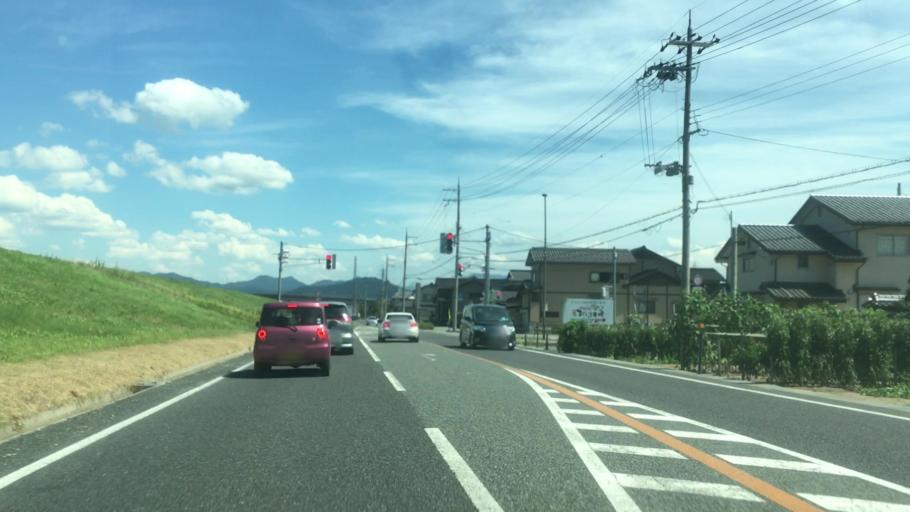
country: JP
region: Hyogo
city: Toyooka
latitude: 35.5589
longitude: 134.8157
